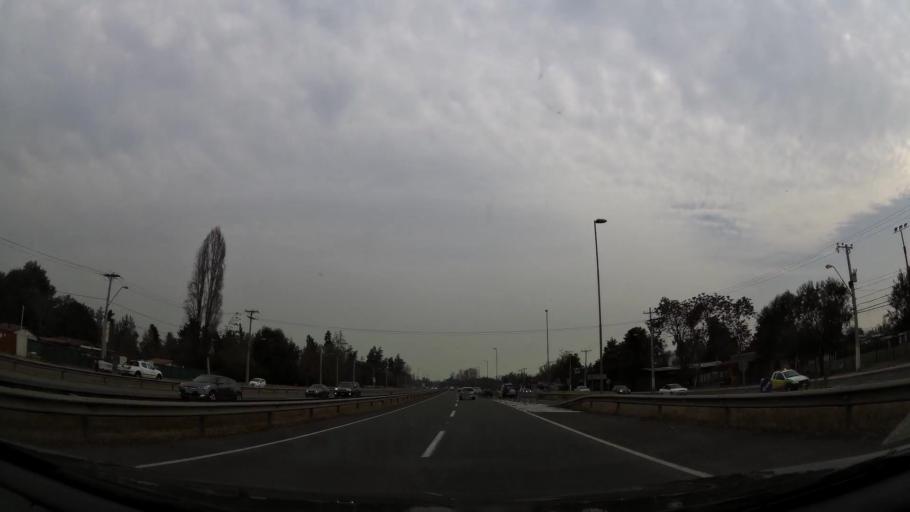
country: CL
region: Santiago Metropolitan
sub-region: Provincia de Chacabuco
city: Chicureo Abajo
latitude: -33.2342
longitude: -70.6938
